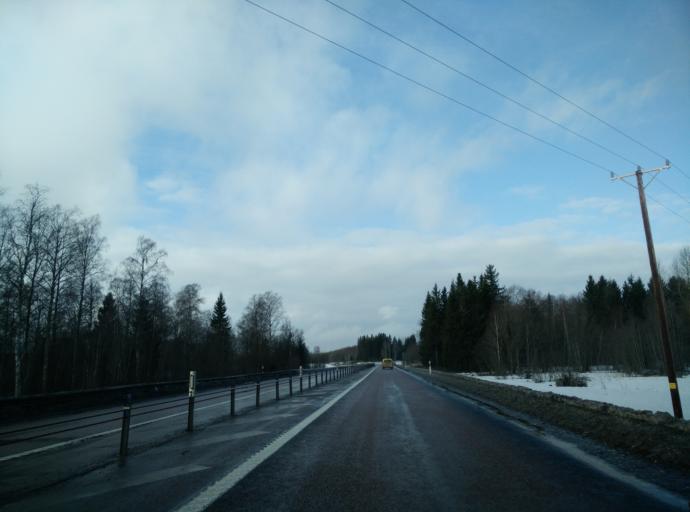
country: SE
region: Gaevleborg
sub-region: Sandvikens Kommun
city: Jarbo
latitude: 60.6107
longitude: 16.6351
